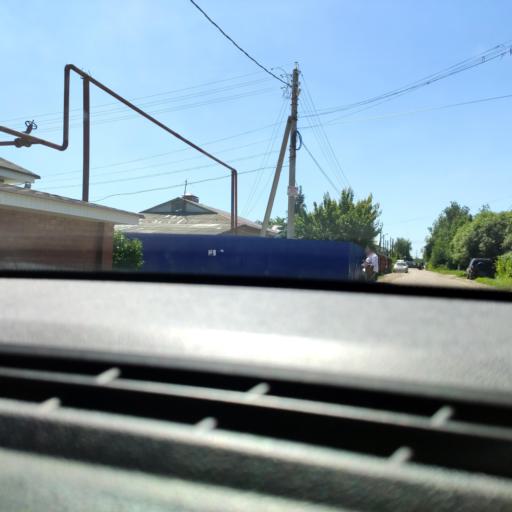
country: RU
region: Samara
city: Tol'yatti
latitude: 53.5635
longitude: 49.3895
